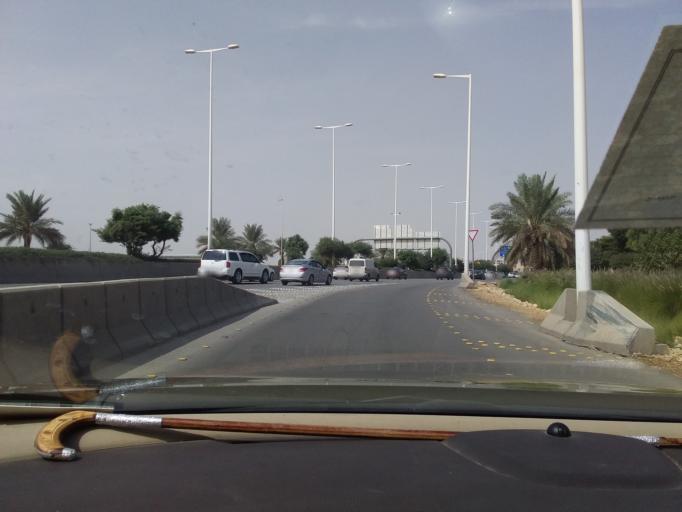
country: SA
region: Ar Riyad
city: Riyadh
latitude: 24.7296
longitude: 46.7098
